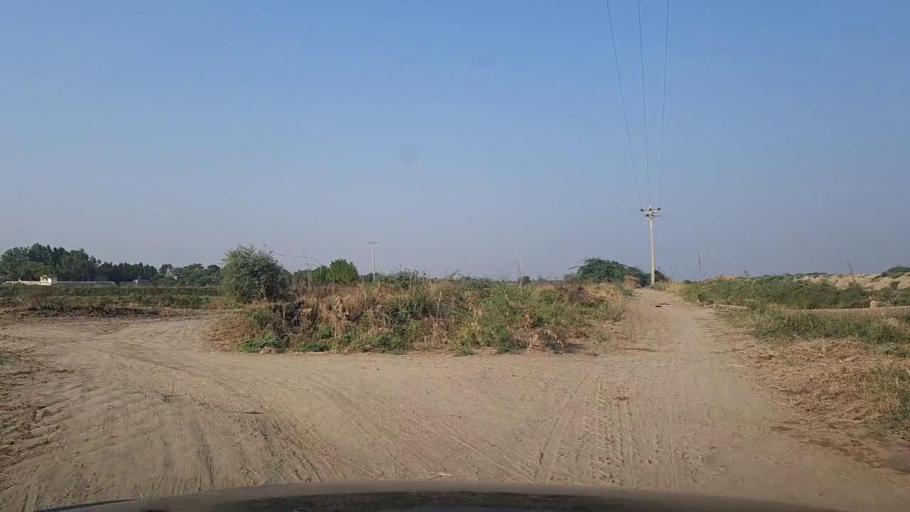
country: PK
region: Sindh
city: Thatta
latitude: 24.7577
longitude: 67.9607
